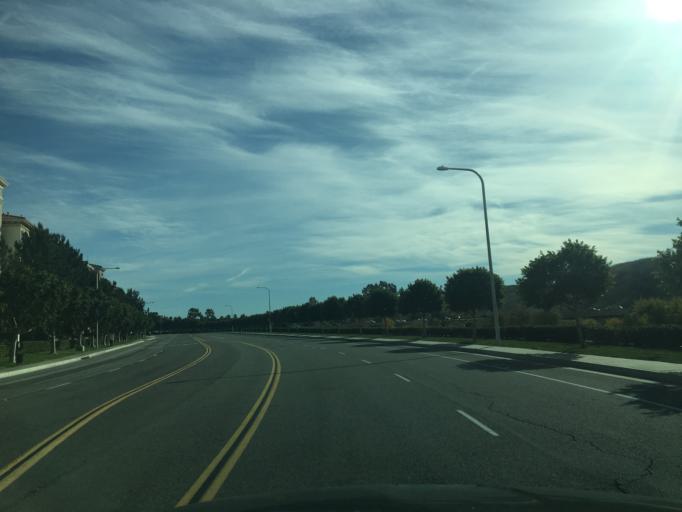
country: US
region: California
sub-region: Orange County
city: Laguna Woods
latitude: 33.6534
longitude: -117.7561
